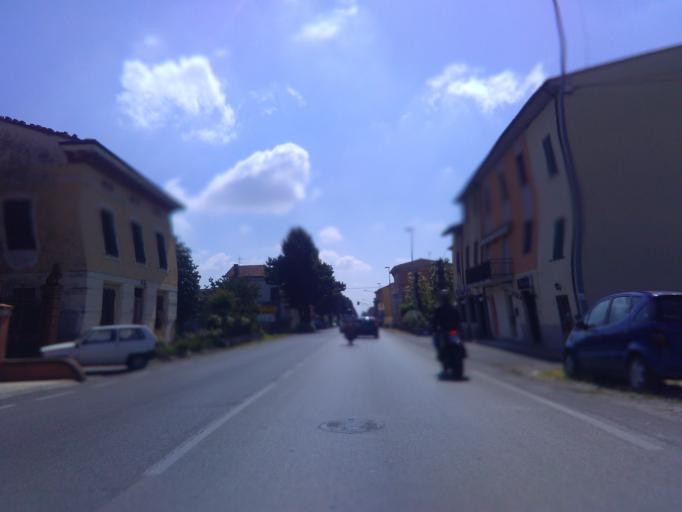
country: IT
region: Tuscany
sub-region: Provincia di Lucca
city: Lucca
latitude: 43.8510
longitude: 10.4560
